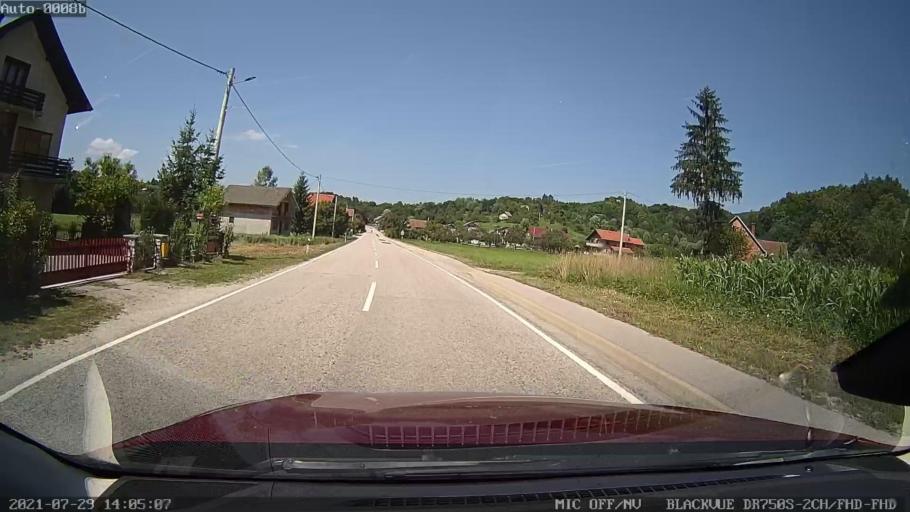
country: HR
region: Varazdinska
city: Lepoglava
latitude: 46.2472
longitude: 15.9594
